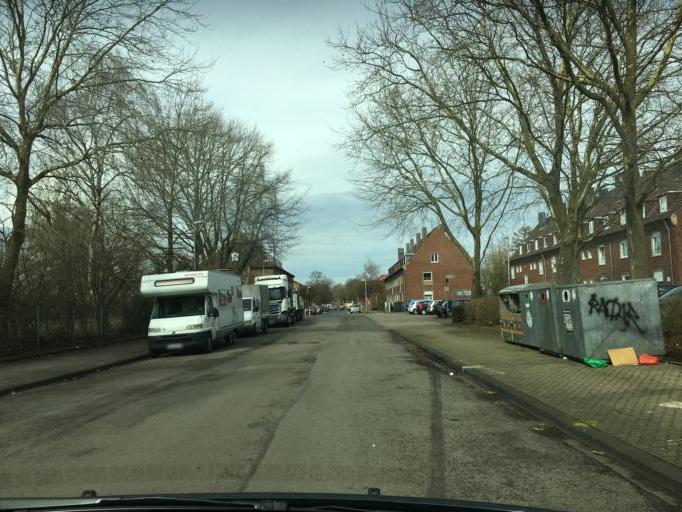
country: DE
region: North Rhine-Westphalia
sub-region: Regierungsbezirk Koln
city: Dueren
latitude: 50.8130
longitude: 6.4974
